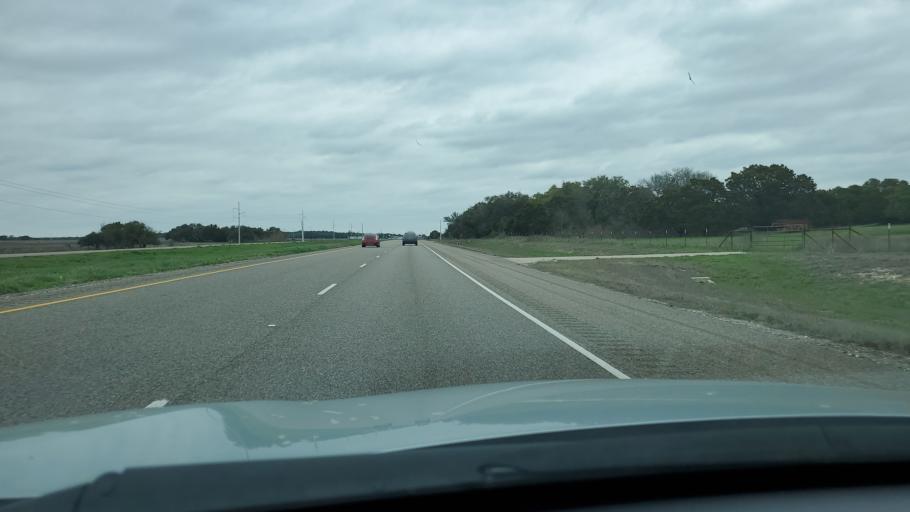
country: US
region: Texas
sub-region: Williamson County
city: Florence
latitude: 30.7738
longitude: -97.7587
